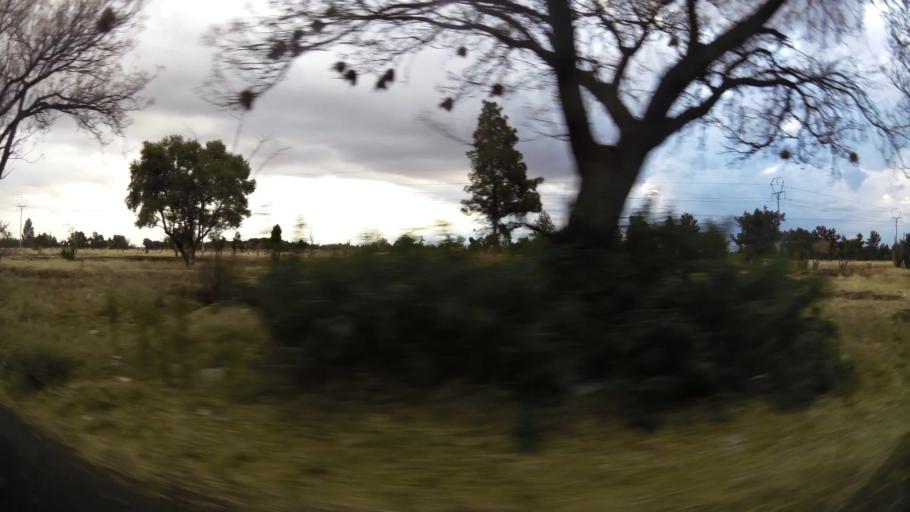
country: ZA
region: Orange Free State
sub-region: Lejweleputswa District Municipality
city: Welkom
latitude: -27.9567
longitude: 26.7194
